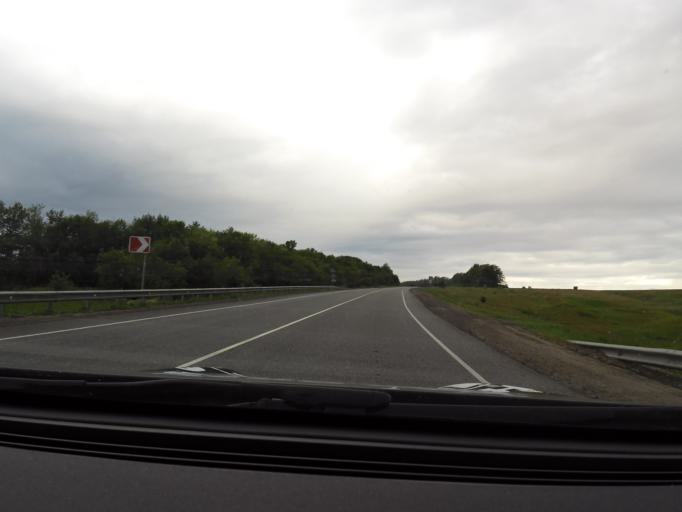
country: RU
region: Chuvashia
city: Kozlovka
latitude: 55.7859
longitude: 48.1516
